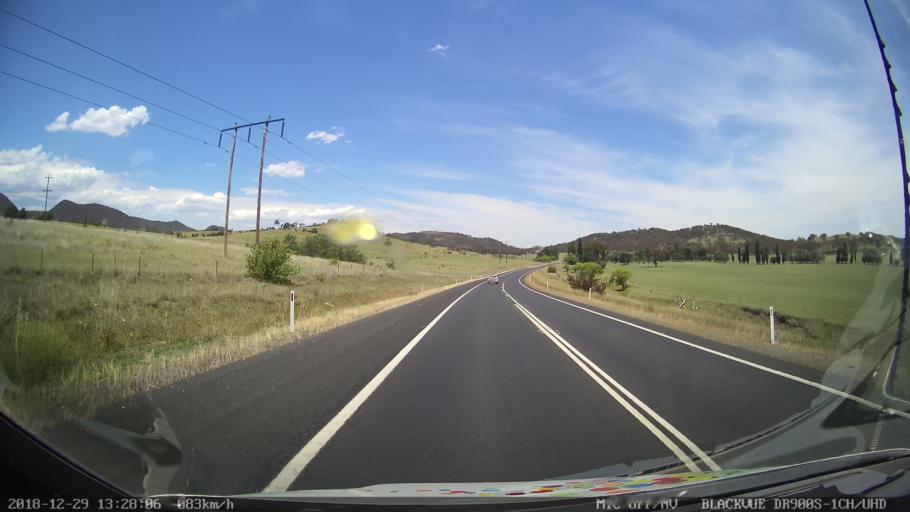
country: AU
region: New South Wales
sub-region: Cooma-Monaro
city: Cooma
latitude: -35.8710
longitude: 149.1612
